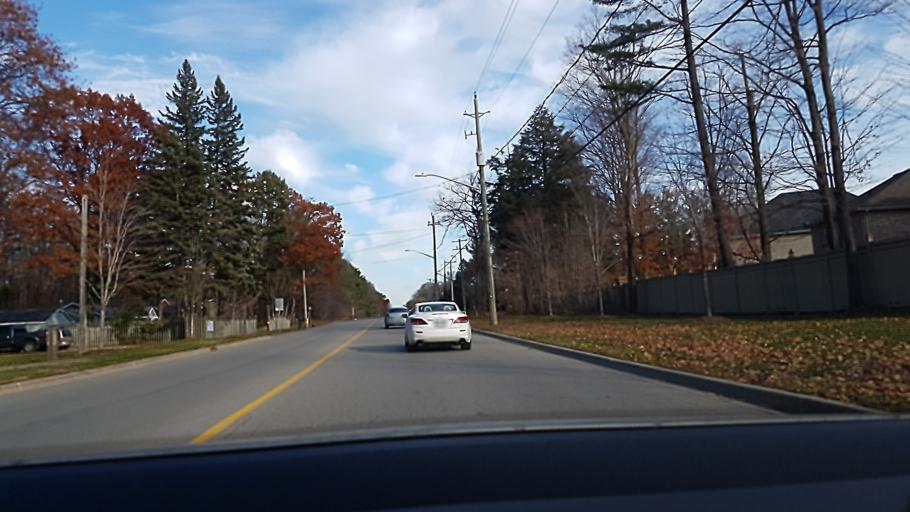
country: CA
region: Ontario
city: Barrie
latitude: 44.3662
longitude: -79.6069
